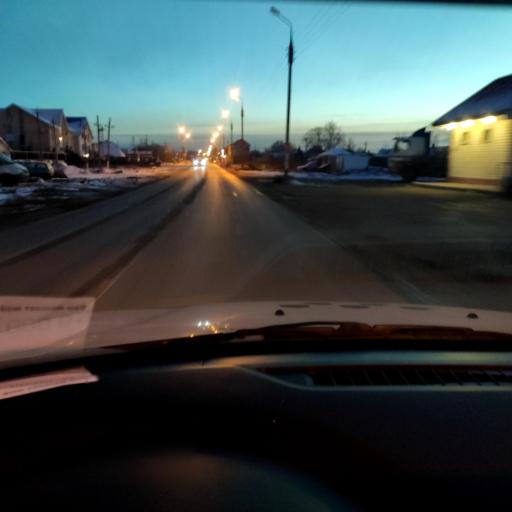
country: RU
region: Samara
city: Tol'yatti
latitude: 53.5685
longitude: 49.3975
